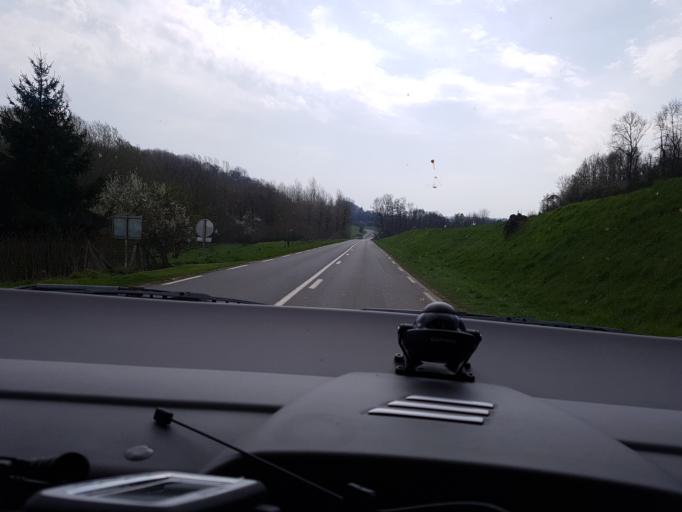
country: FR
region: Picardie
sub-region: Departement de l'Aisne
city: Coucy-le-Chateau-Auffrique
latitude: 49.4878
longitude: 3.3368
